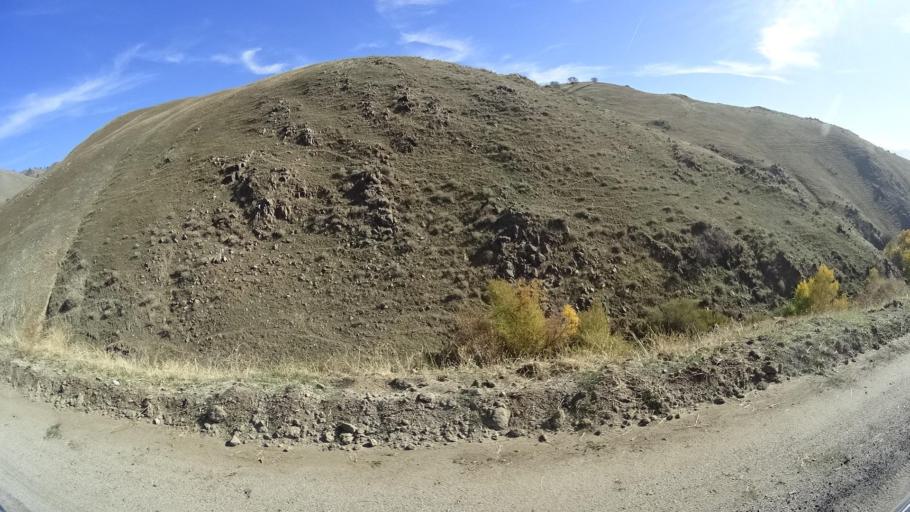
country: US
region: California
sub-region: Kern County
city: Arvin
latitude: 35.4139
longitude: -118.7472
